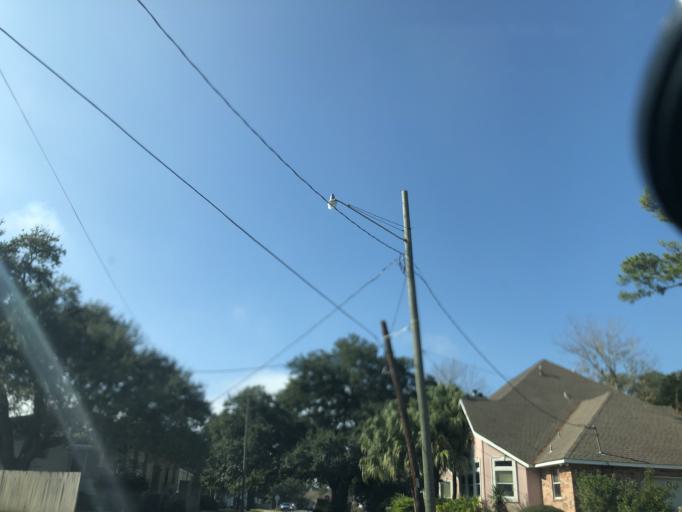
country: US
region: Louisiana
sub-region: Jefferson Parish
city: Metairie
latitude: 29.9820
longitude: -90.1511
